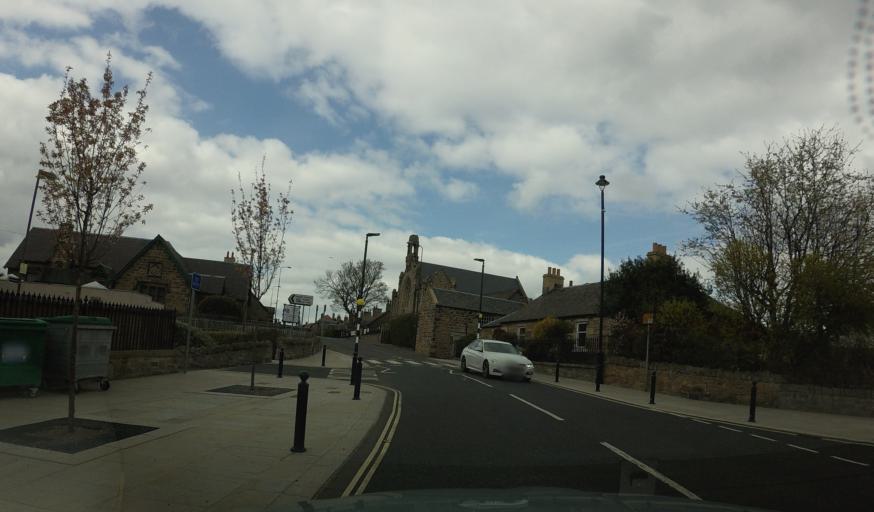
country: GB
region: Scotland
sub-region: Midlothian
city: Gorebridge
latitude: 55.8424
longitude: -3.0474
